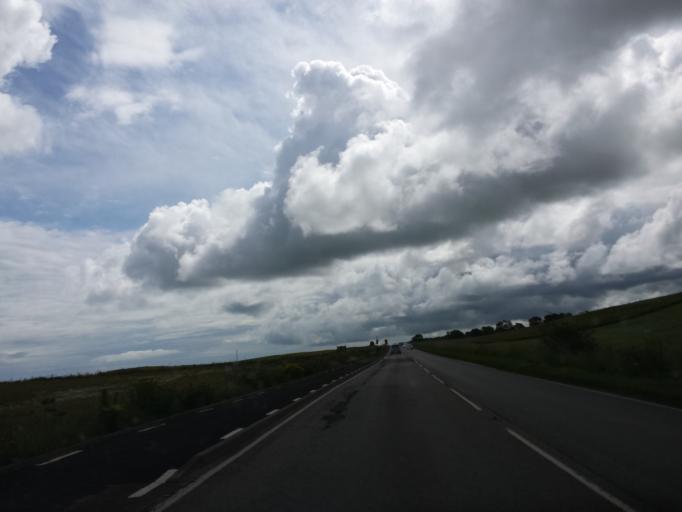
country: GB
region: Scotland
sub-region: Fife
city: Strathkinness
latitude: 56.3586
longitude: -2.8671
